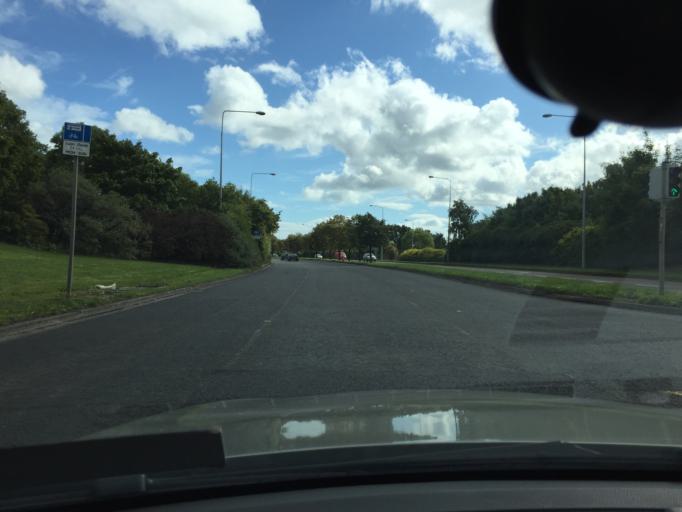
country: IE
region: Leinster
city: Crumlin
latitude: 53.3431
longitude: -6.3216
